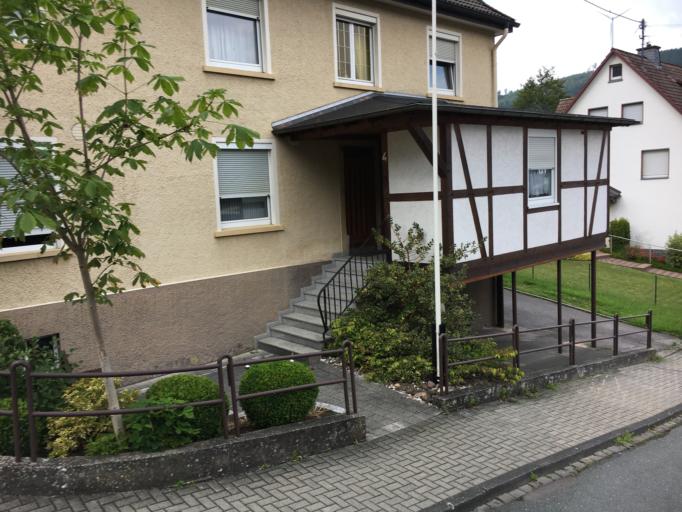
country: DE
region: North Rhine-Westphalia
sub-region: Regierungsbezirk Arnsberg
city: Lennestadt
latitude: 51.1217
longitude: 8.0643
